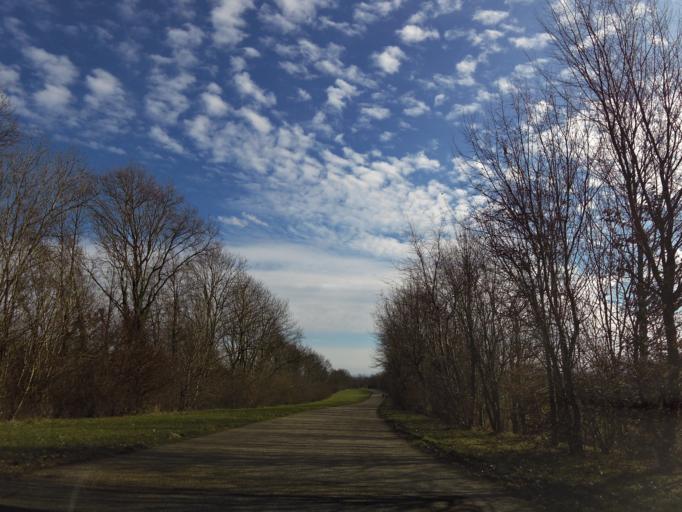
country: NL
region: Limburg
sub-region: Gemeente Simpelveld
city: Simpelveld
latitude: 50.8484
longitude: 5.9807
